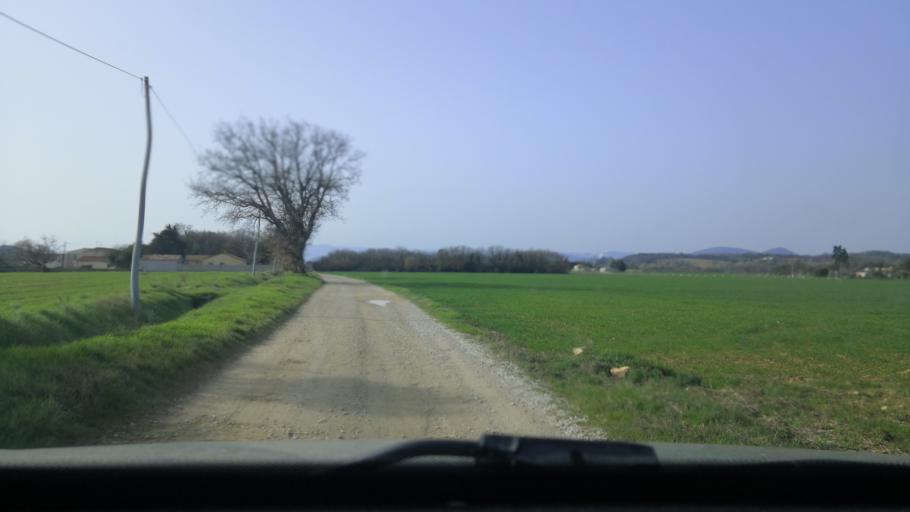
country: FR
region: Rhone-Alpes
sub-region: Departement de la Drome
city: La Begude-de-Mazenc
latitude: 44.5560
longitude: 4.8945
